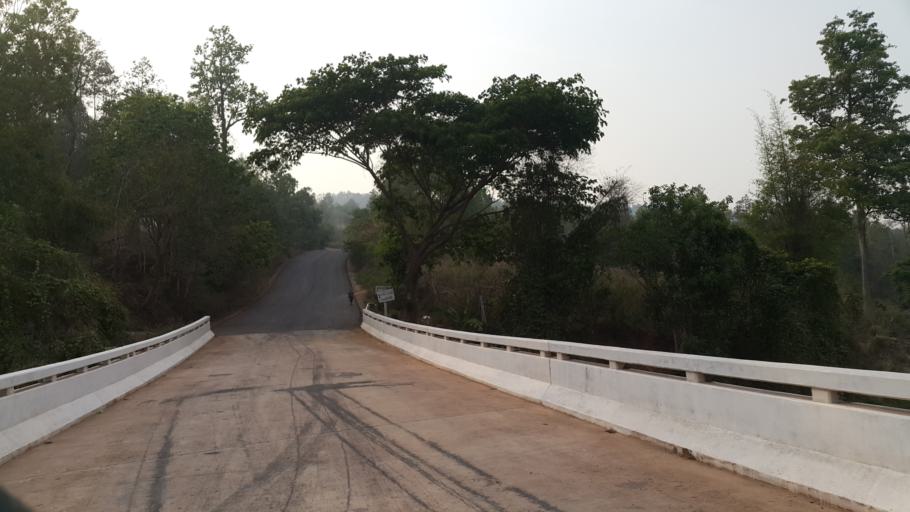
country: TH
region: Chiang Mai
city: Mae On
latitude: 18.7507
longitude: 99.3017
